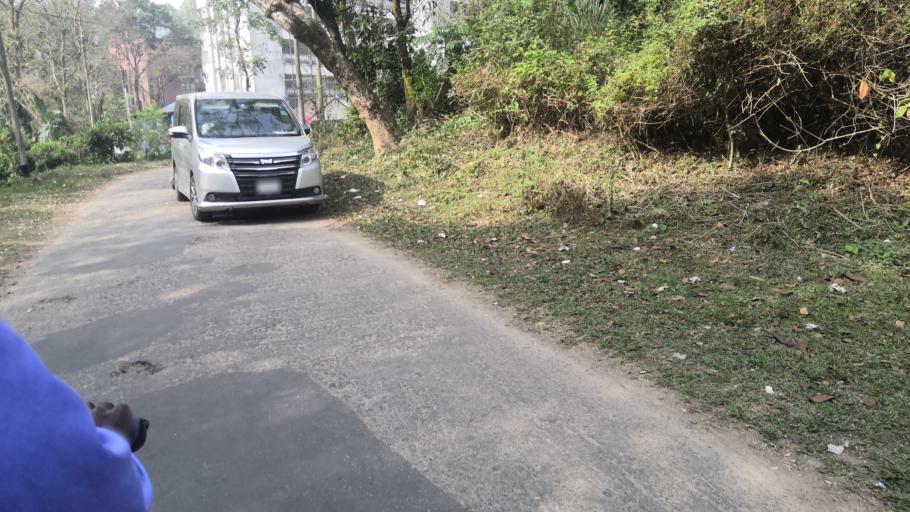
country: BD
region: Chittagong
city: Chittagong
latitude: 22.4721
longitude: 91.7864
